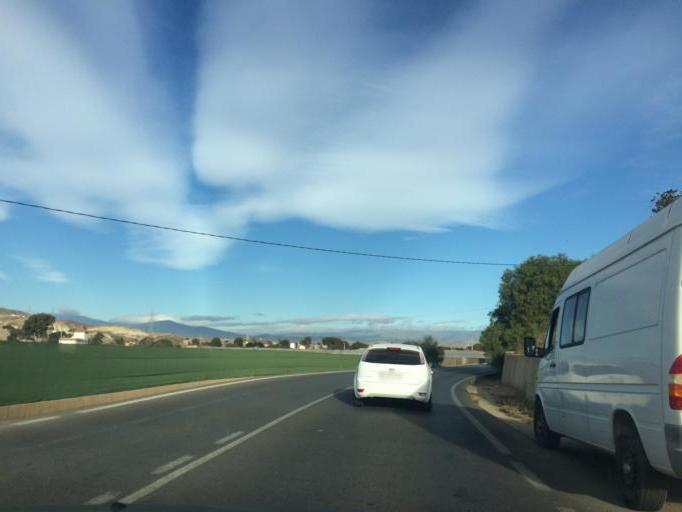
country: ES
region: Andalusia
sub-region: Provincia de Almeria
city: Viator
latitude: 36.8945
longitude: -2.4311
